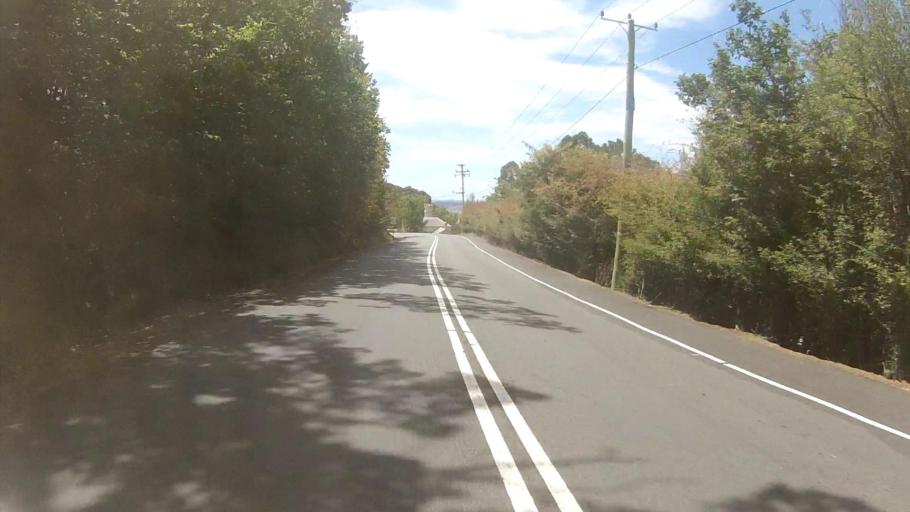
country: AU
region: Tasmania
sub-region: Kingborough
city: Taroona
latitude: -42.9589
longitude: 147.3358
